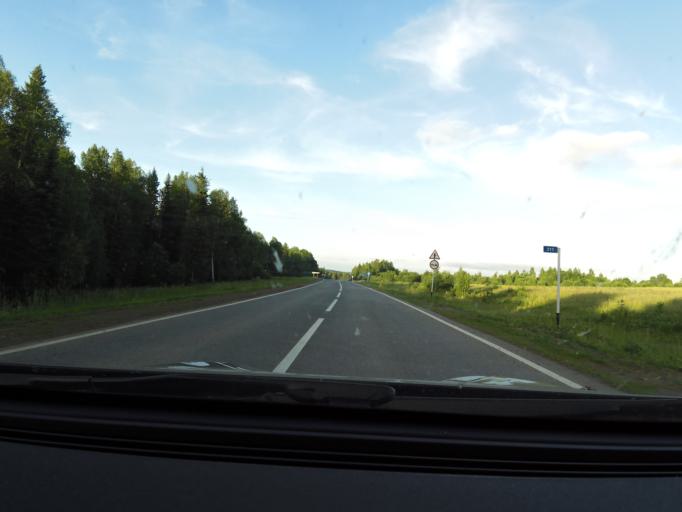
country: RU
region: Perm
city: Siva
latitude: 58.5394
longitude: 53.9365
